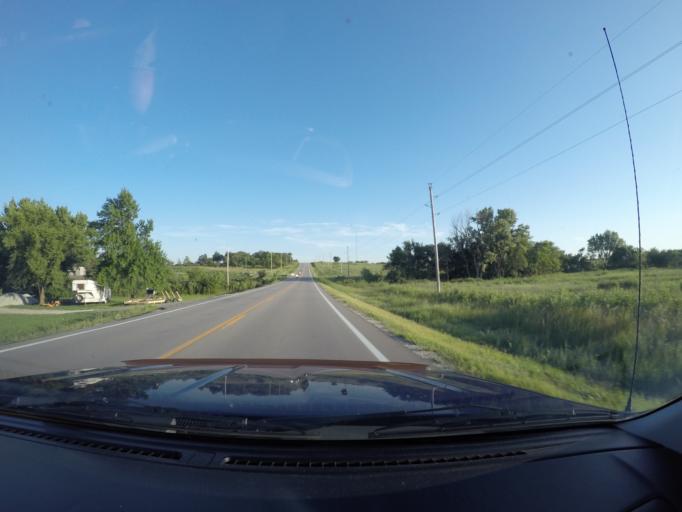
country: US
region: Kansas
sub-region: Pottawatomie County
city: Wamego
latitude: 39.1110
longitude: -96.2893
